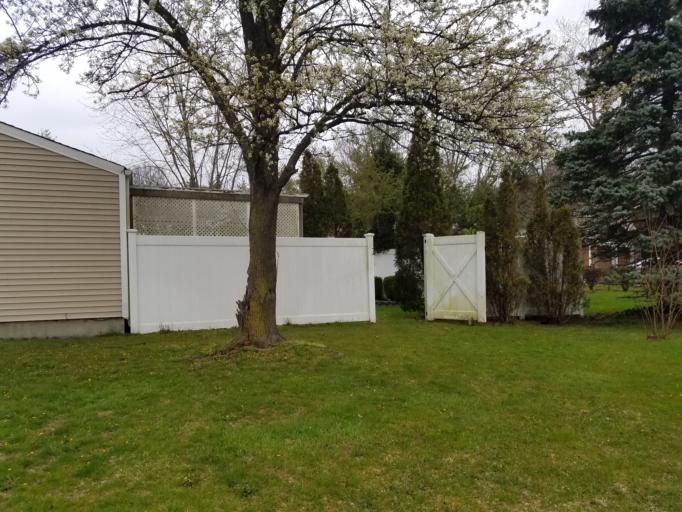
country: US
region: New York
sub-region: Suffolk County
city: Islandia
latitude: 40.8230
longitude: -73.1643
